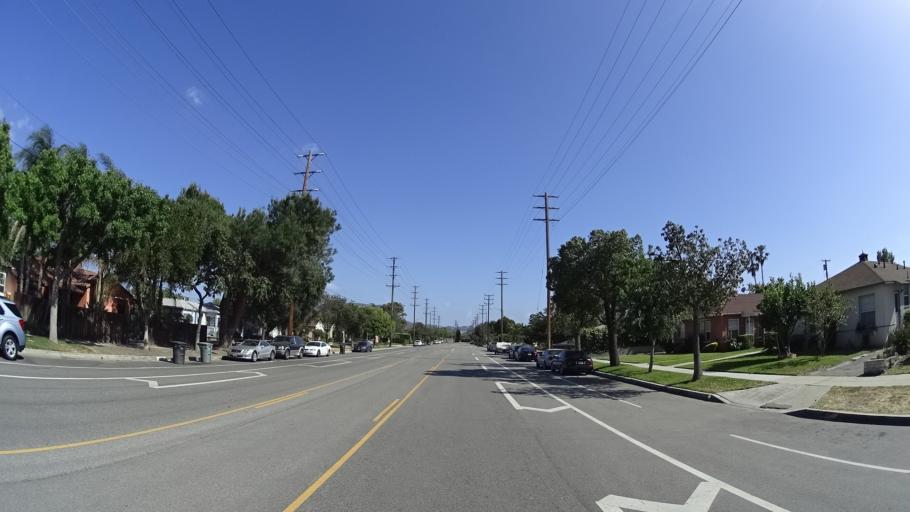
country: US
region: California
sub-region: Los Angeles County
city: North Hollywood
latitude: 34.1715
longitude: -118.3575
